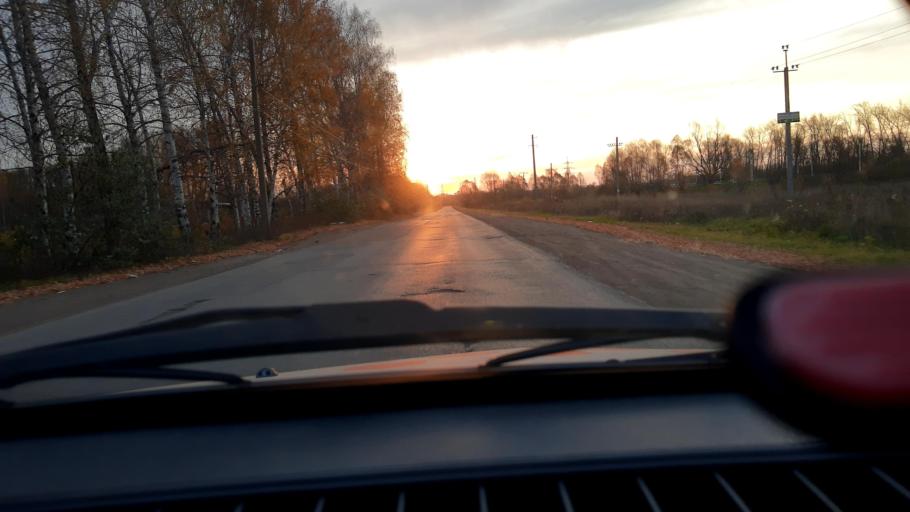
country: RU
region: Bashkortostan
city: Ufa
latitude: 54.8104
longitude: 56.1645
